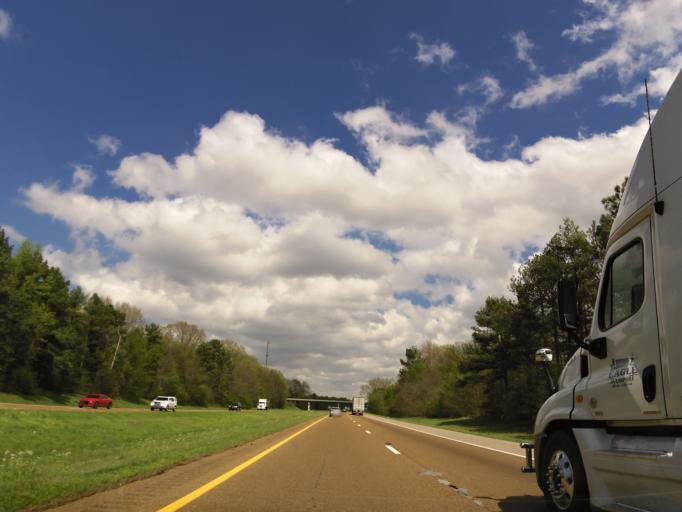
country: US
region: Tennessee
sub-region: Tipton County
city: Mason
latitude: 35.3700
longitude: -89.4723
